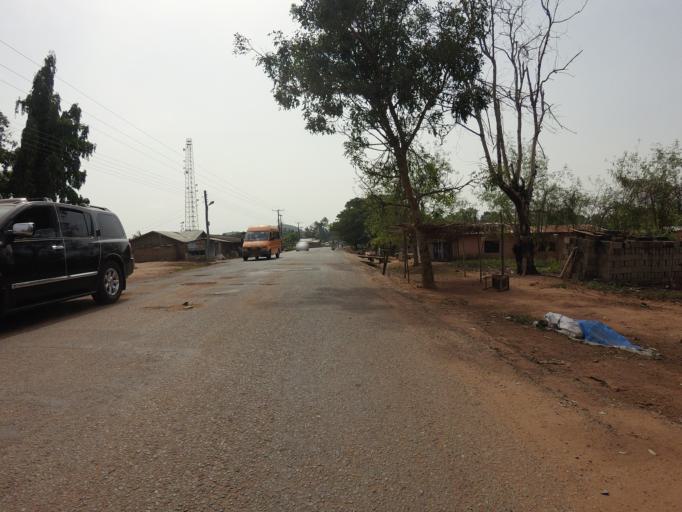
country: GH
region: Volta
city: Ho
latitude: 6.3784
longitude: 0.1877
